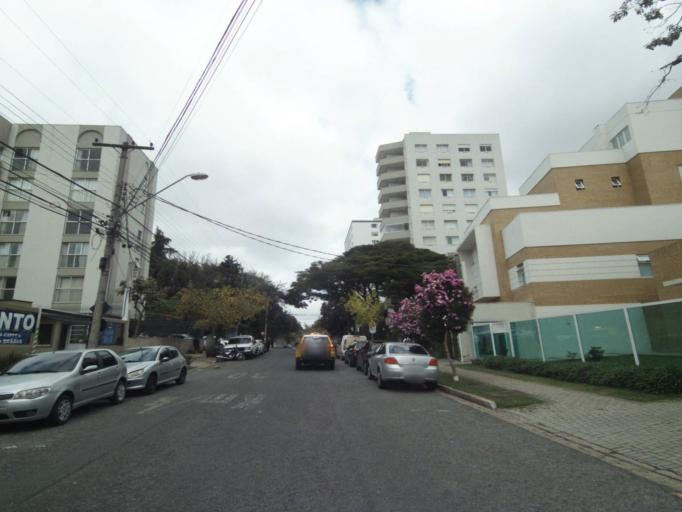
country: BR
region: Parana
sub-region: Curitiba
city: Curitiba
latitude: -25.4154
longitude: -49.2655
